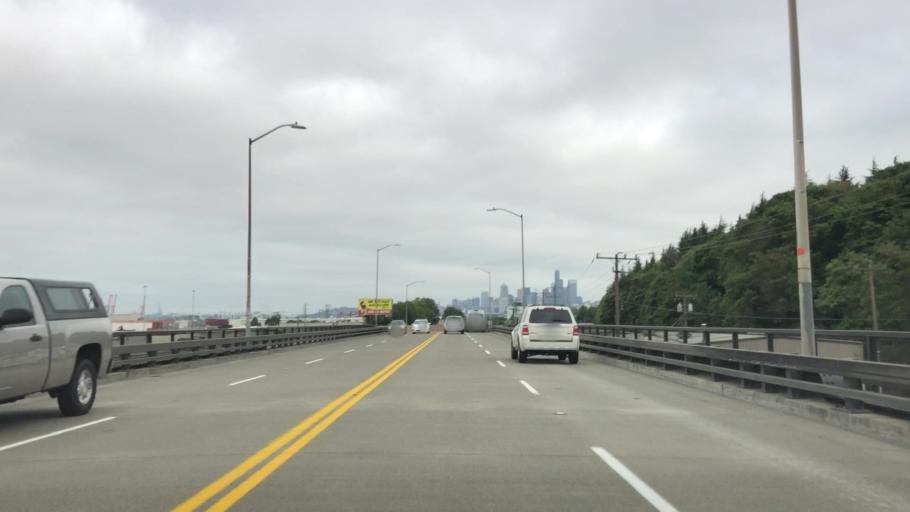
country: US
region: Washington
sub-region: King County
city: White Center
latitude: 47.5559
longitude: -122.3223
